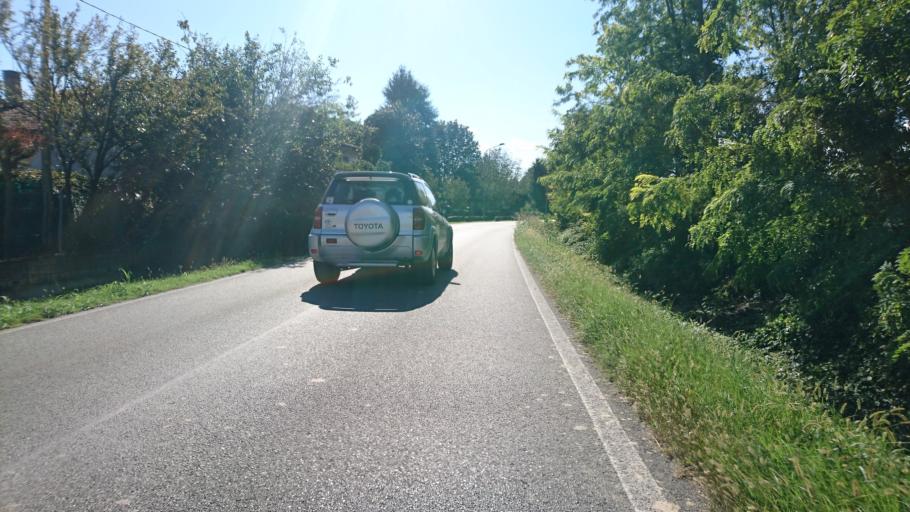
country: IT
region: Veneto
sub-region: Provincia di Venezia
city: Vigonovo
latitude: 45.3995
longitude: 12.0025
